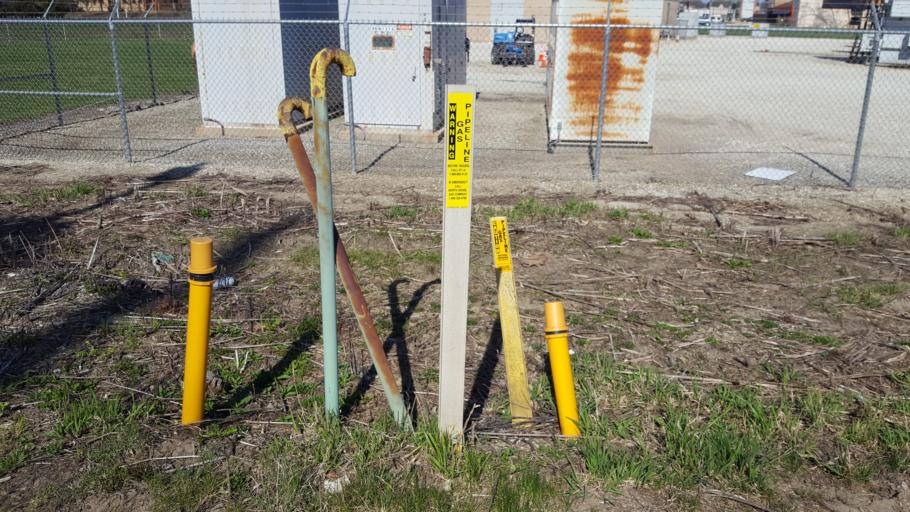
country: US
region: Illinois
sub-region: Lake County
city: Deerfield
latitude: 42.1523
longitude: -87.8412
